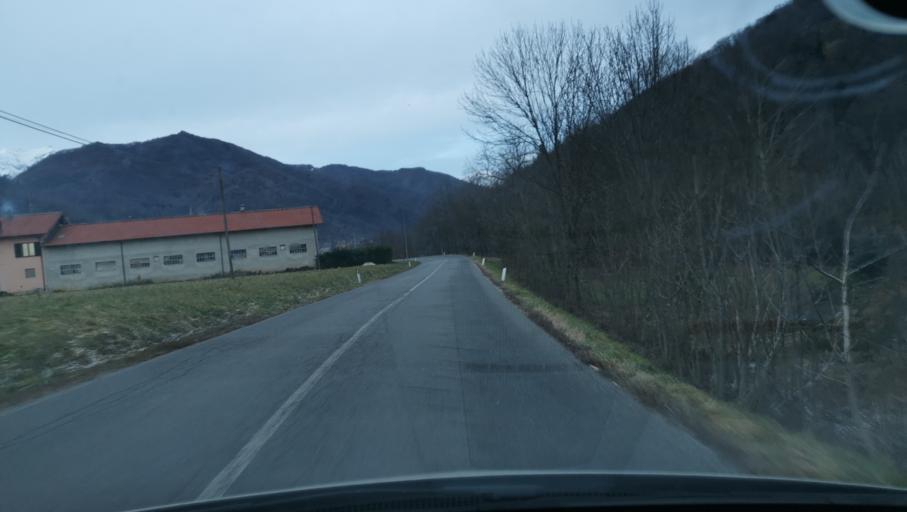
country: IT
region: Piedmont
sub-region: Provincia di Cuneo
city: Monterosso Grana
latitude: 44.4098
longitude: 7.3311
